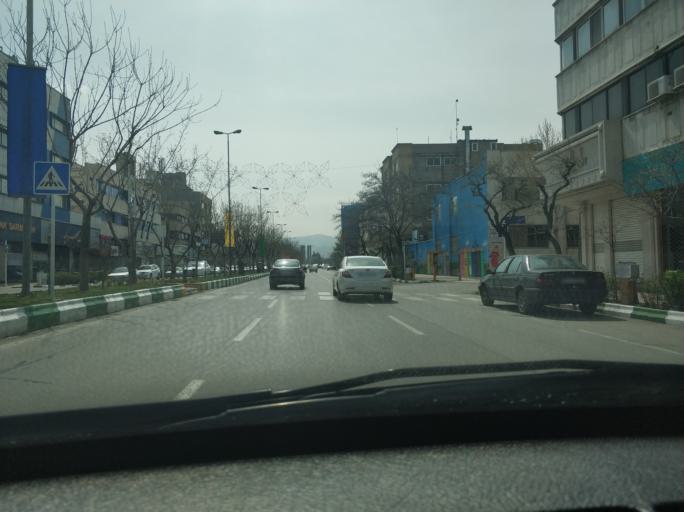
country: IR
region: Razavi Khorasan
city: Mashhad
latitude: 36.3030
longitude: 59.5646
